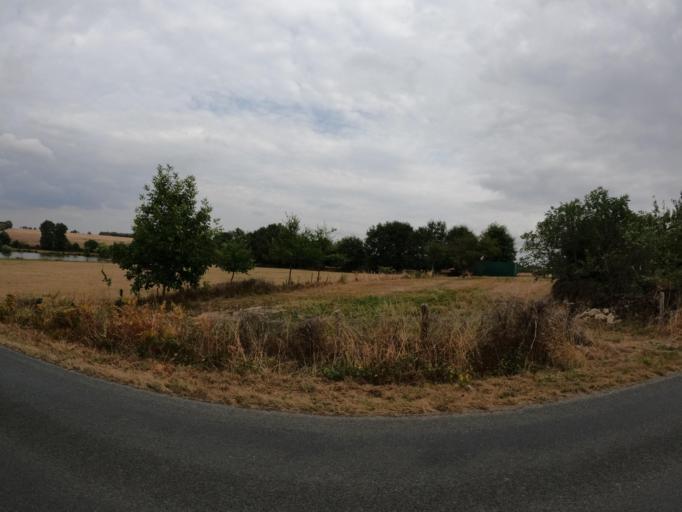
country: FR
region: Pays de la Loire
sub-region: Departement de la Vendee
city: Les Landes-Genusson
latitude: 46.9720
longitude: -1.1132
